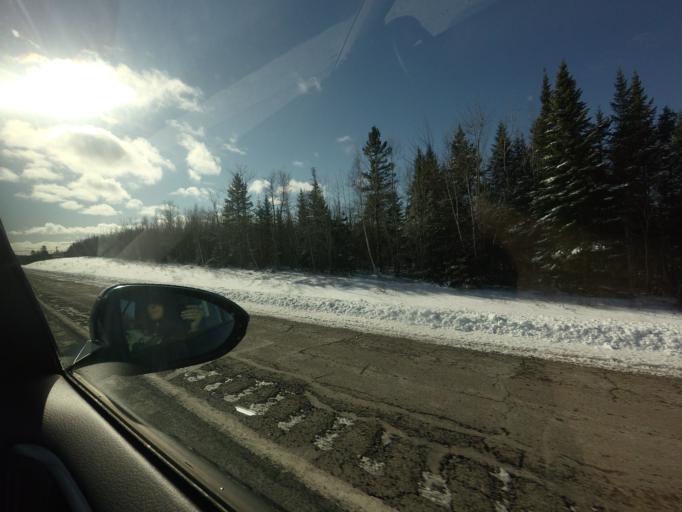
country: CA
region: New Brunswick
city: Fredericton
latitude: 45.8948
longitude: -66.6481
